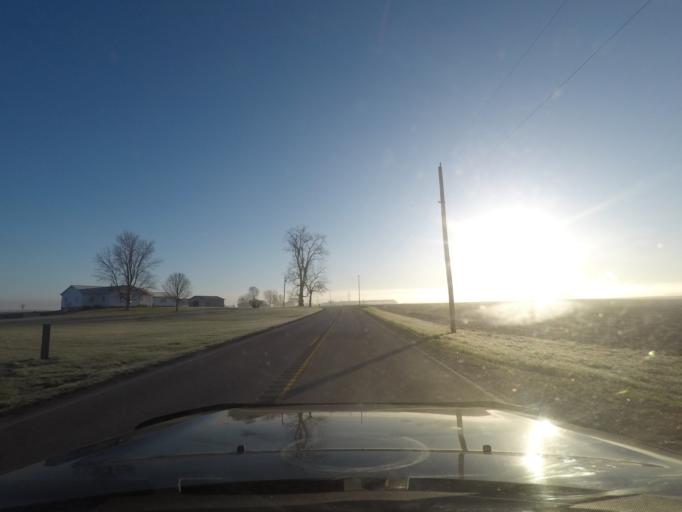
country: US
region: Indiana
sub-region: Elkhart County
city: Wakarusa
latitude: 41.5162
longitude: -85.9779
